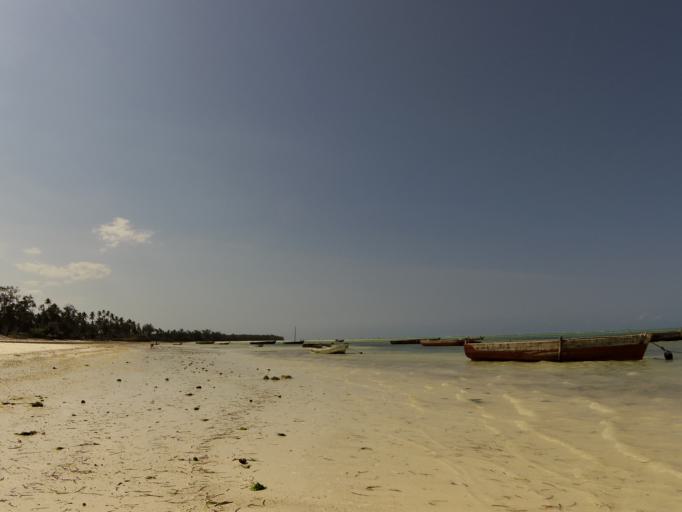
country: TZ
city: Kiwengwa
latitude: -6.0924
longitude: 39.4262
